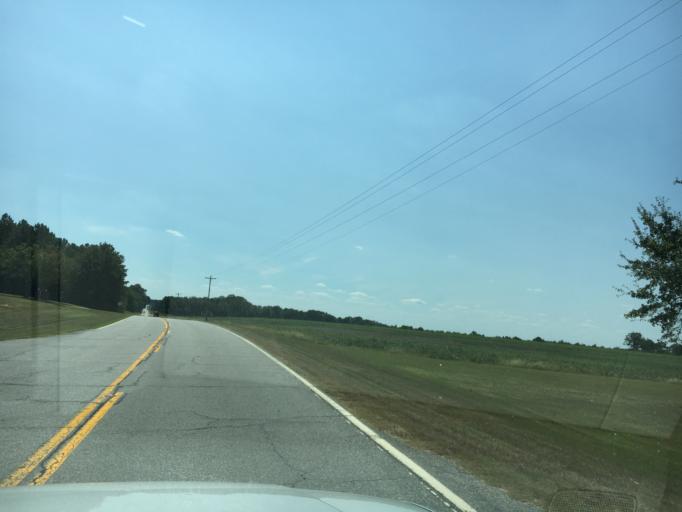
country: US
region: South Carolina
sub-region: Lexington County
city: Batesburg
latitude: 33.7913
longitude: -81.6443
